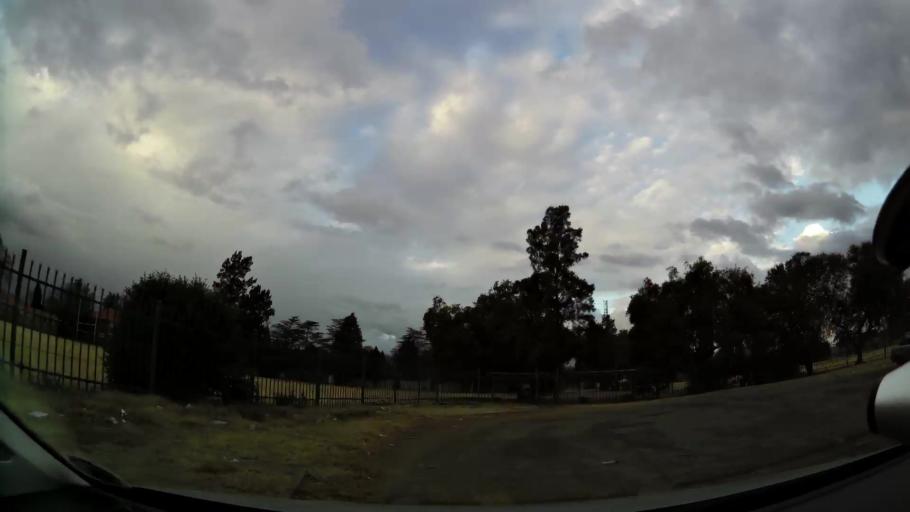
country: ZA
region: Orange Free State
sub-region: Lejweleputswa District Municipality
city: Welkom
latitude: -27.9626
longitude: 26.7409
